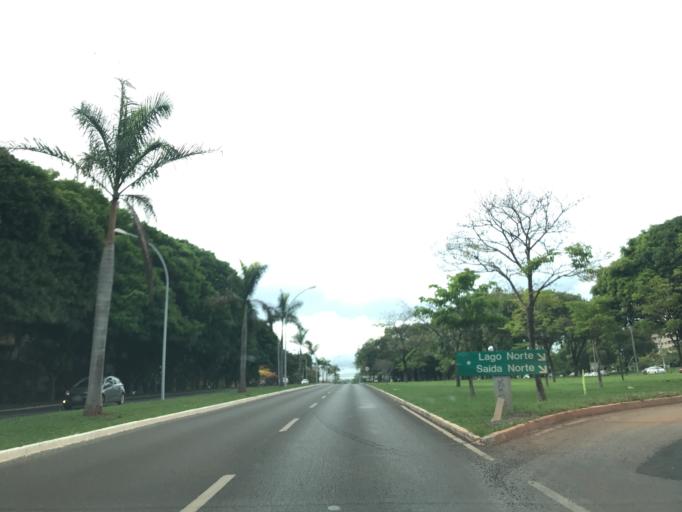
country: BR
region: Federal District
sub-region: Brasilia
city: Brasilia
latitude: -15.7408
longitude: -47.8904
